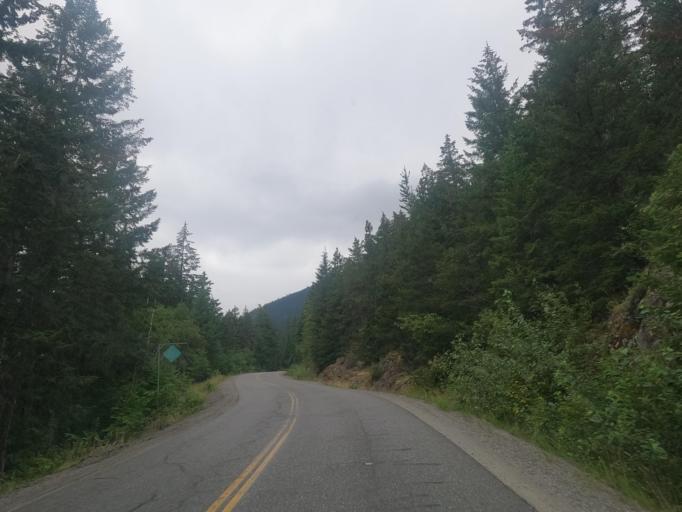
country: CA
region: British Columbia
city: Pemberton
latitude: 50.3038
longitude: -122.5747
